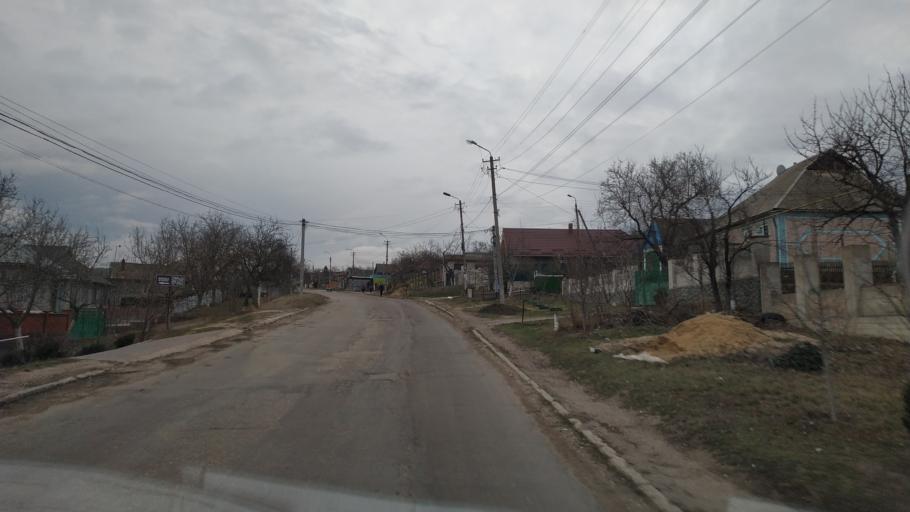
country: MD
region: Causeni
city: Causeni
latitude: 46.6314
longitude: 29.4024
